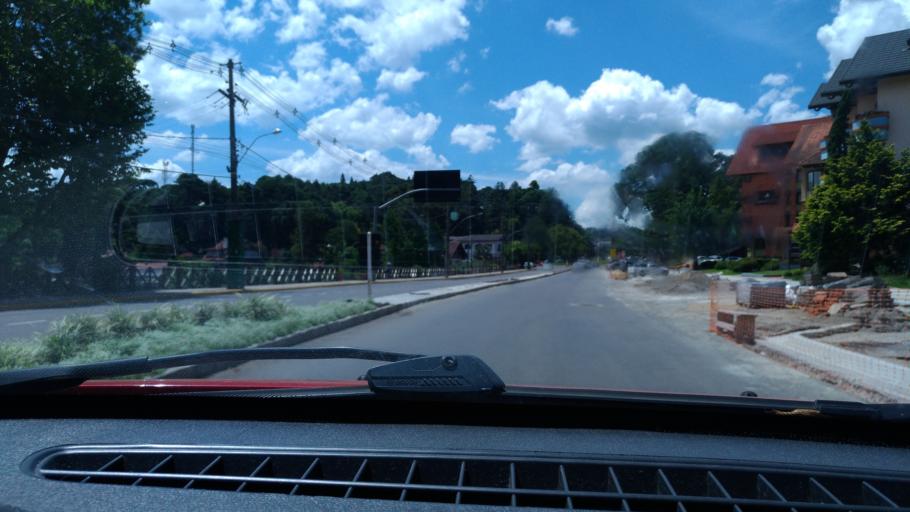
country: BR
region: Rio Grande do Sul
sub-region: Canela
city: Canela
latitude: -29.3876
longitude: -50.8744
